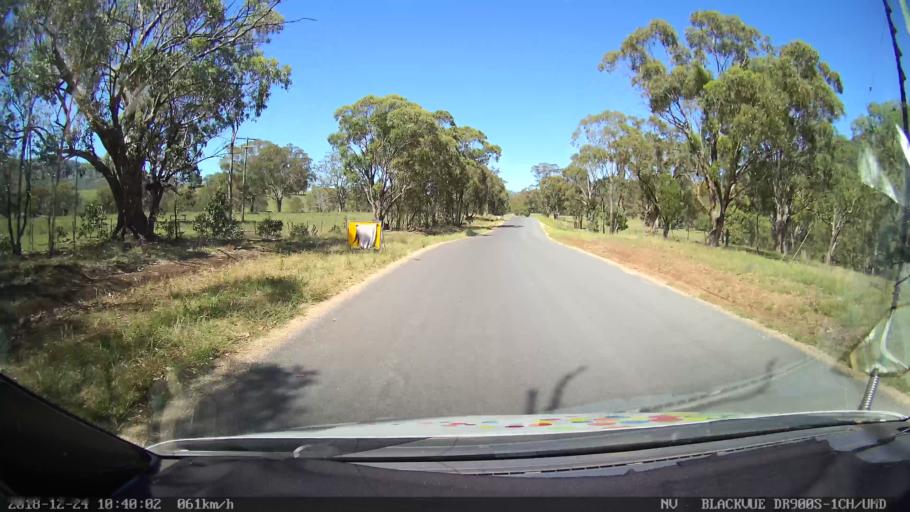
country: AU
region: New South Wales
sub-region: Upper Hunter Shire
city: Merriwa
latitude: -31.8593
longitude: 150.4709
